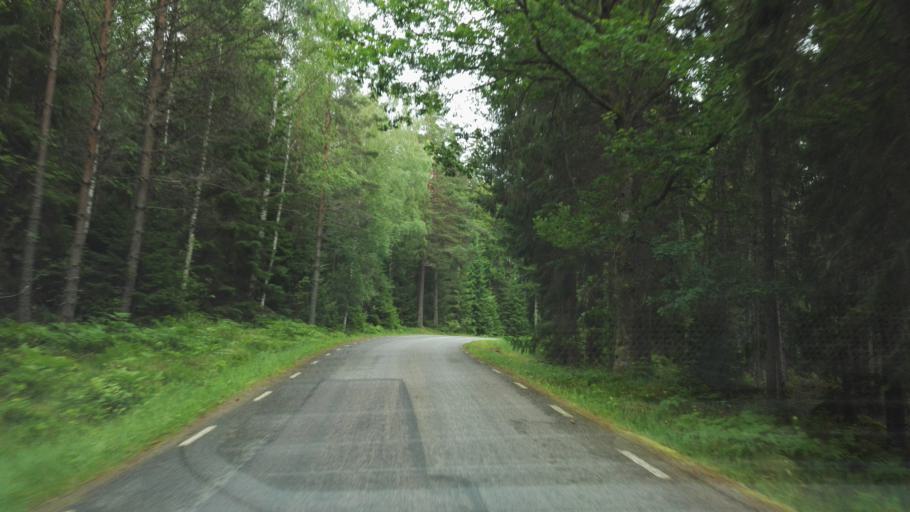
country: SE
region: Kronoberg
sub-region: Vaxjo Kommun
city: Rottne
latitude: 57.1500
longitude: 14.8096
